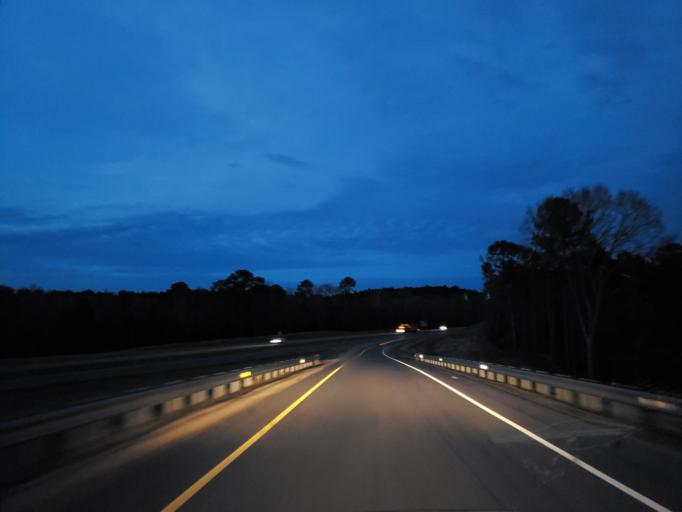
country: US
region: Alabama
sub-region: Greene County
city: Eutaw
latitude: 32.8684
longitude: -87.9229
